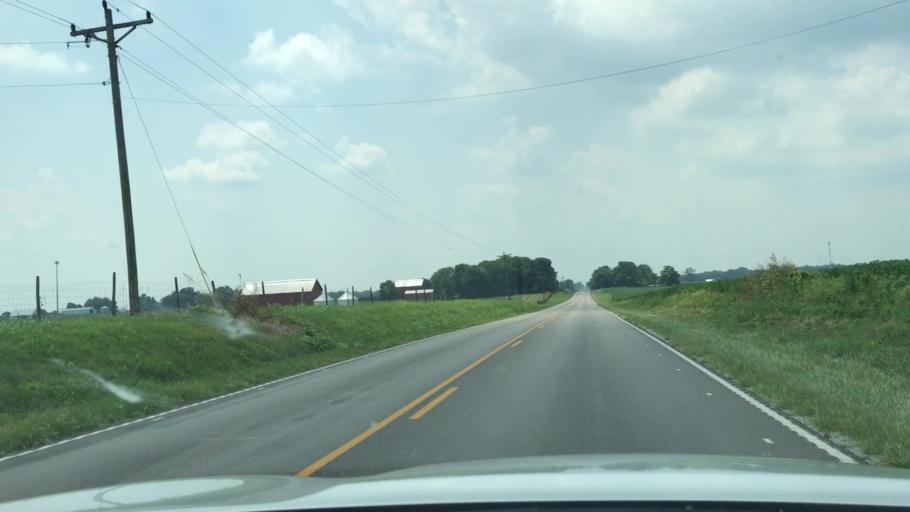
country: US
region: Kentucky
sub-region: Todd County
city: Guthrie
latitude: 36.7029
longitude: -87.1128
